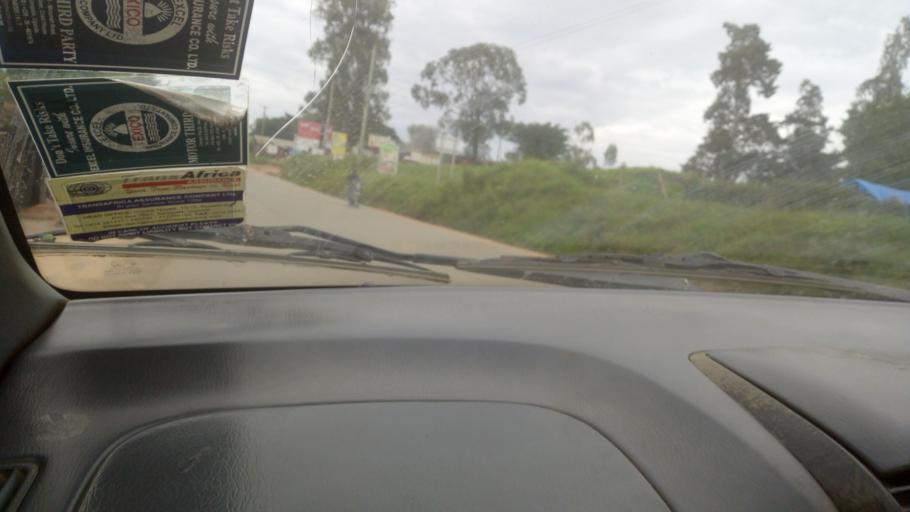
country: UG
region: Western Region
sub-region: Mbarara District
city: Mbarara
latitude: -0.6030
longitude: 30.6501
